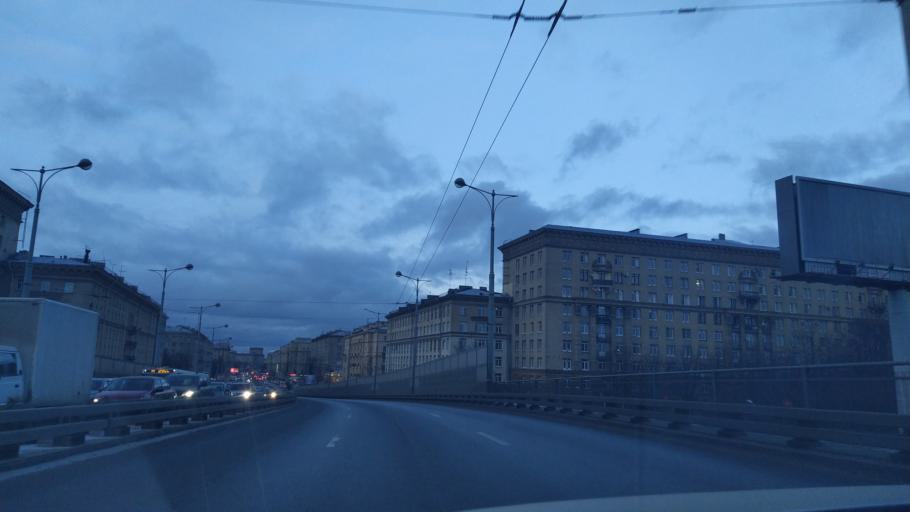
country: RU
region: St.-Petersburg
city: Avtovo
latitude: 59.8645
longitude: 30.2613
